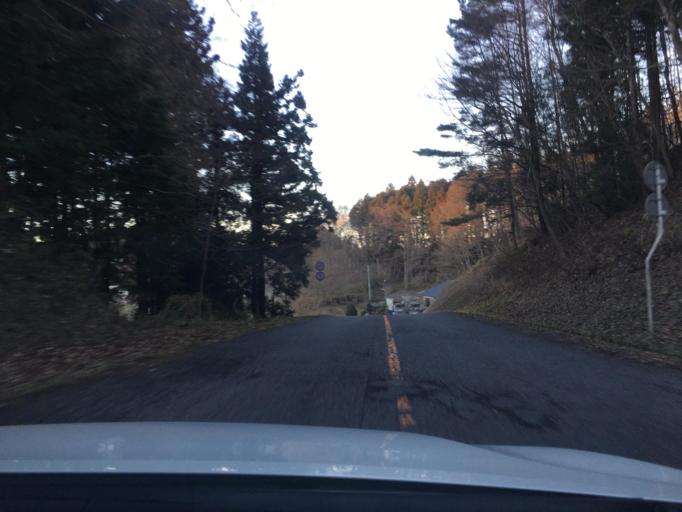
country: JP
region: Fukushima
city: Miharu
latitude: 37.4602
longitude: 140.4951
